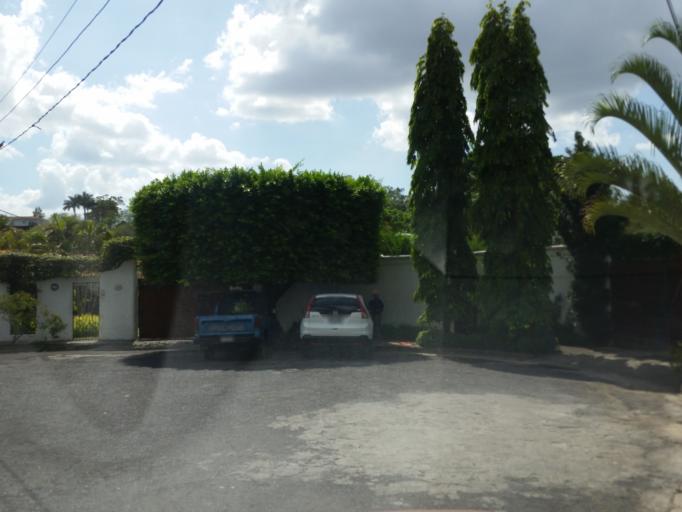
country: NI
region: Managua
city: Managua
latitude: 12.0824
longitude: -86.2468
